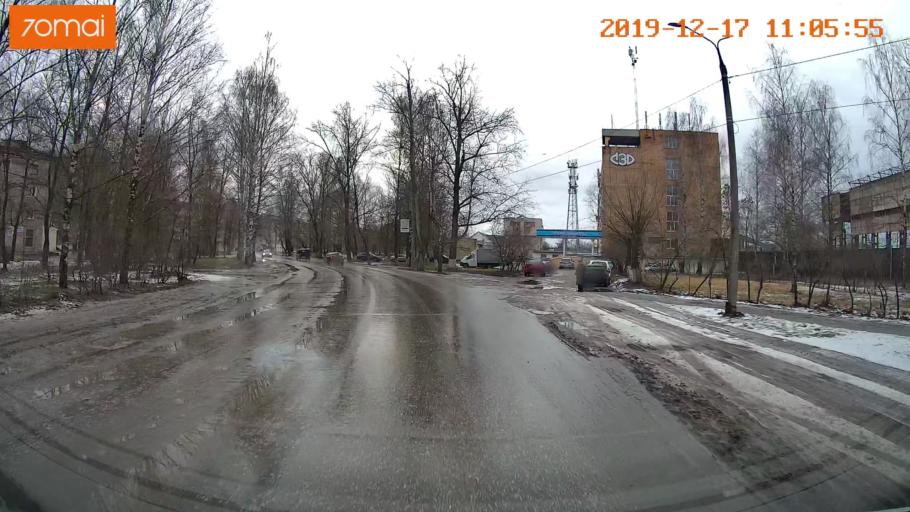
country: RU
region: Vladimir
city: Gus'-Khrustal'nyy
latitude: 55.6181
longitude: 40.6429
